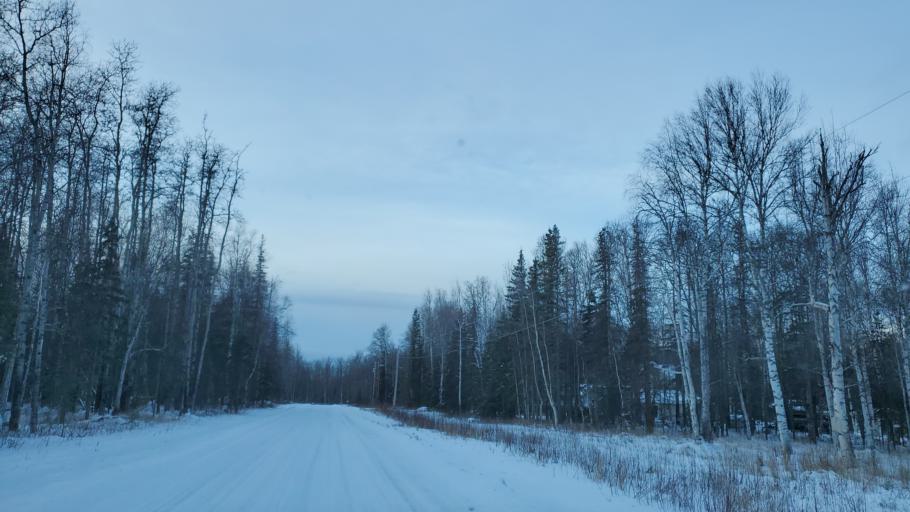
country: US
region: Alaska
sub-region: Matanuska-Susitna Borough
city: Lakes
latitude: 61.6716
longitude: -149.2814
